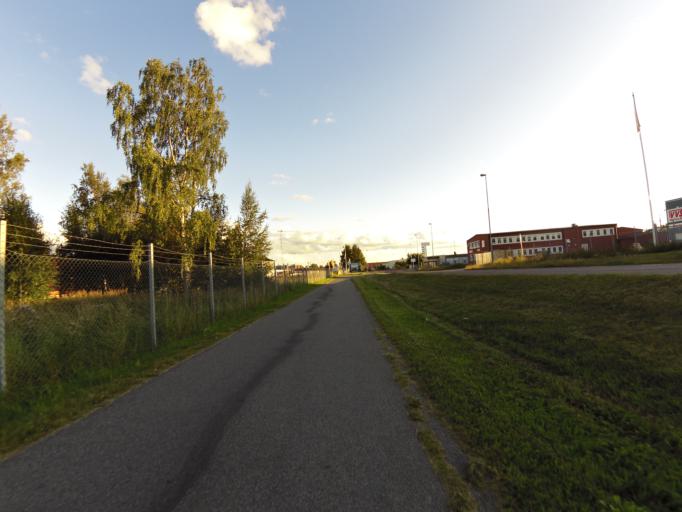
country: SE
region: Gaevleborg
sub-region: Gavle Kommun
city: Gavle
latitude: 60.6891
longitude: 17.1541
